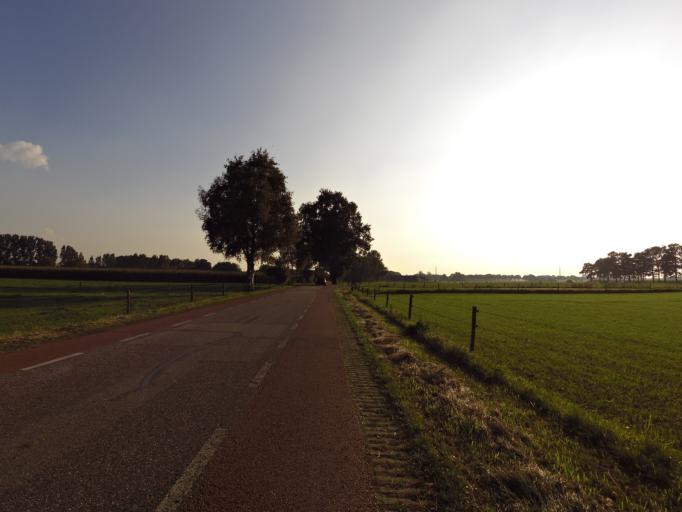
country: NL
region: Gelderland
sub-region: Oude IJsselstreek
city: Wisch
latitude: 51.8920
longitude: 6.4445
